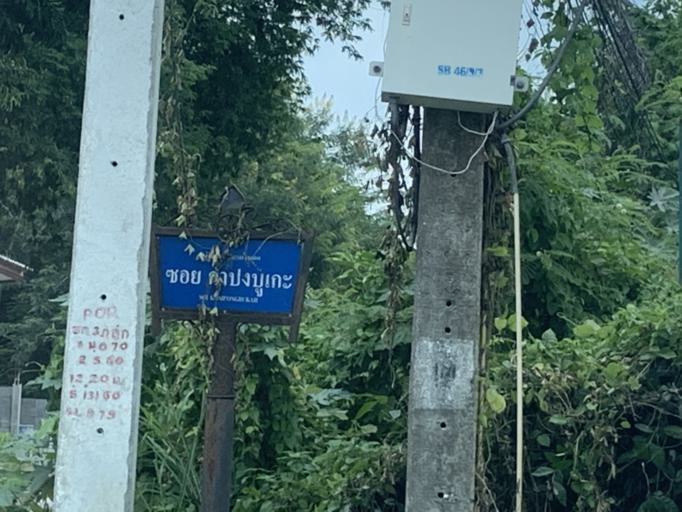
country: TH
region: Yala
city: Yala
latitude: 6.5194
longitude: 101.2886
